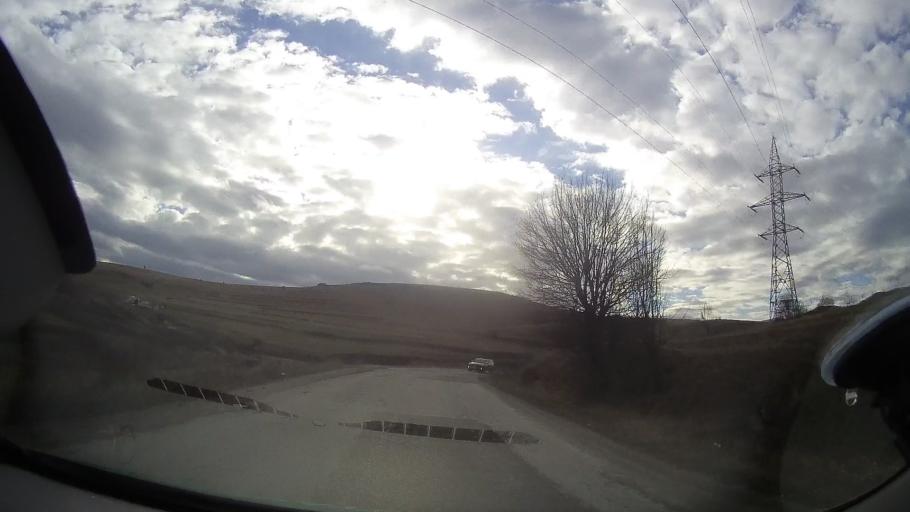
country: RO
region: Cluj
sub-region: Comuna Baisoara
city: Baisoara
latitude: 46.5968
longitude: 23.4644
